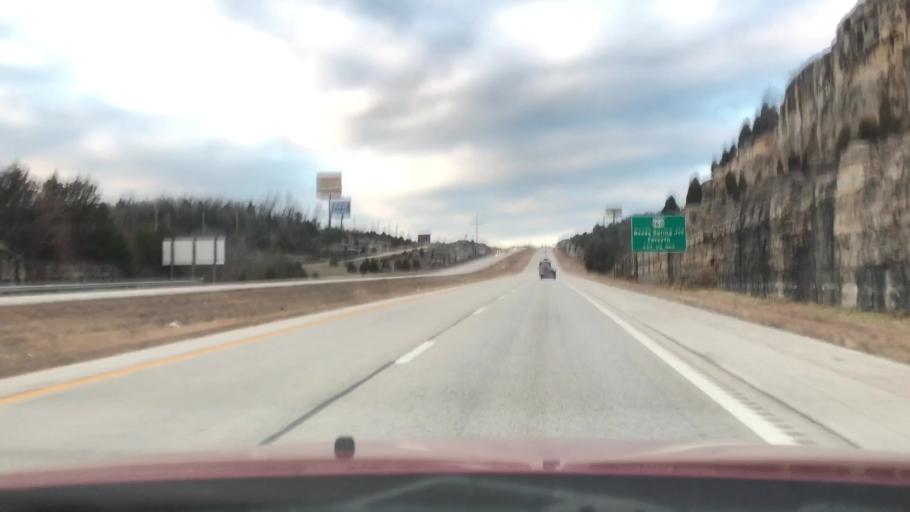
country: US
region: Missouri
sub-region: Taney County
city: Merriam Woods
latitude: 36.7369
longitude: -93.2212
